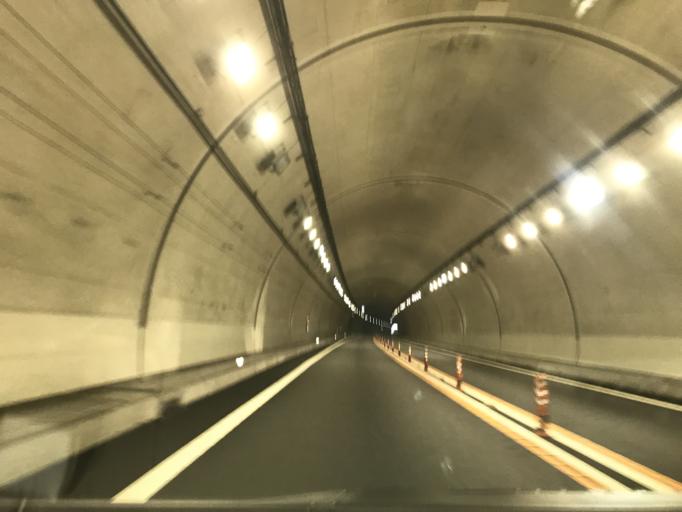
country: JP
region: Fukuoka
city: Kanda
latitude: 33.7768
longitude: 130.9703
